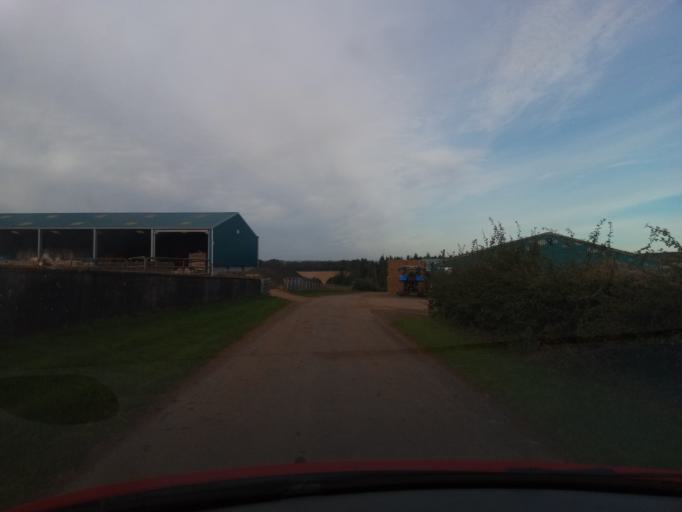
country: GB
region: Scotland
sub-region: The Scottish Borders
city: Kelso
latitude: 55.5810
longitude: -2.3686
